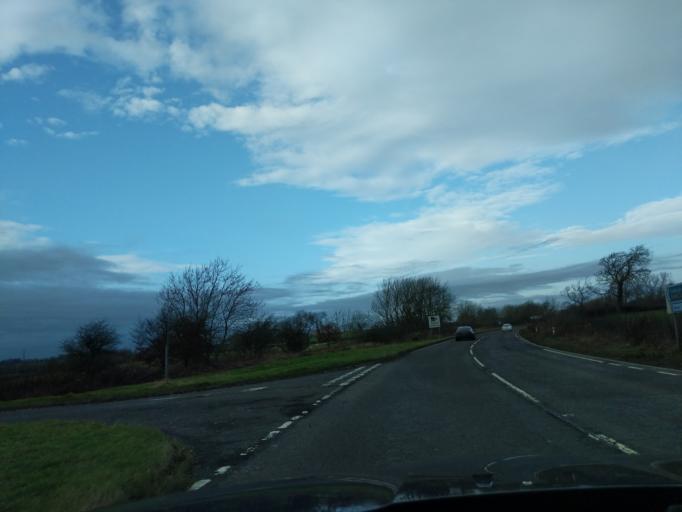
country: GB
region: England
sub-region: Northumberland
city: Meldon
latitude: 55.0792
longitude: -1.8043
